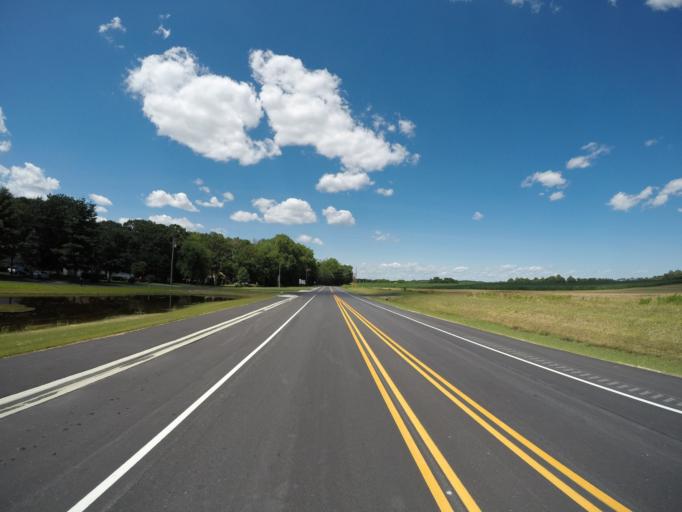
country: US
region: Delaware
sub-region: Sussex County
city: Milford
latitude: 38.9286
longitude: -75.4099
